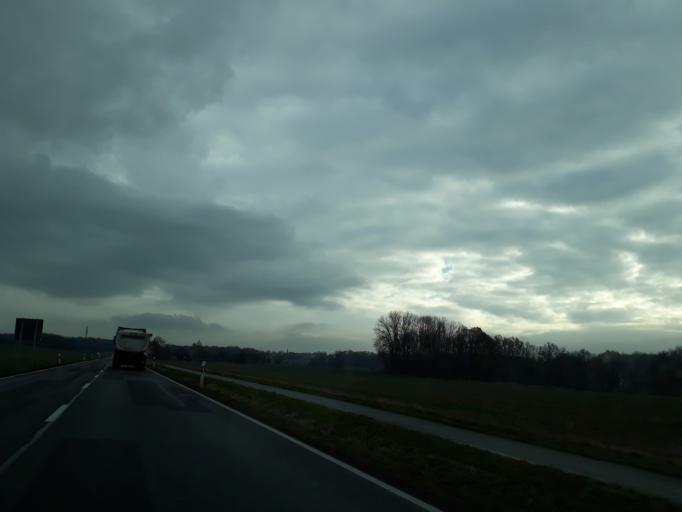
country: DE
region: Saxony
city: Hochkirch
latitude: 51.1369
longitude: 14.5989
